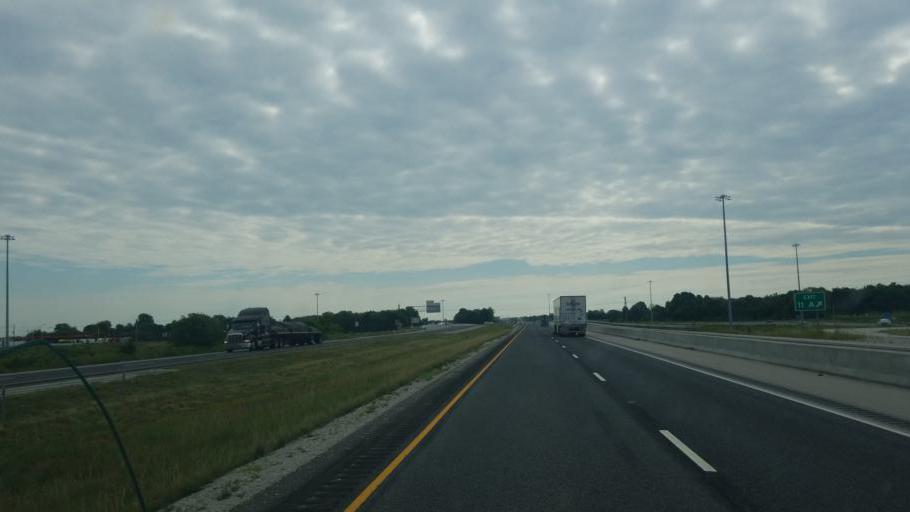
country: US
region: Indiana
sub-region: Vigo County
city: Terre Haute
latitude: 39.4305
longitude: -87.3367
